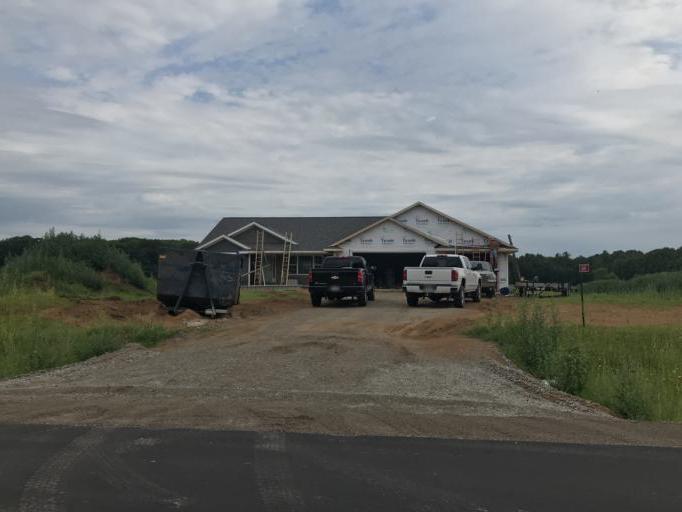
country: US
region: Wisconsin
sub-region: Brown County
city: Suamico
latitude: 44.6851
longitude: -88.0960
